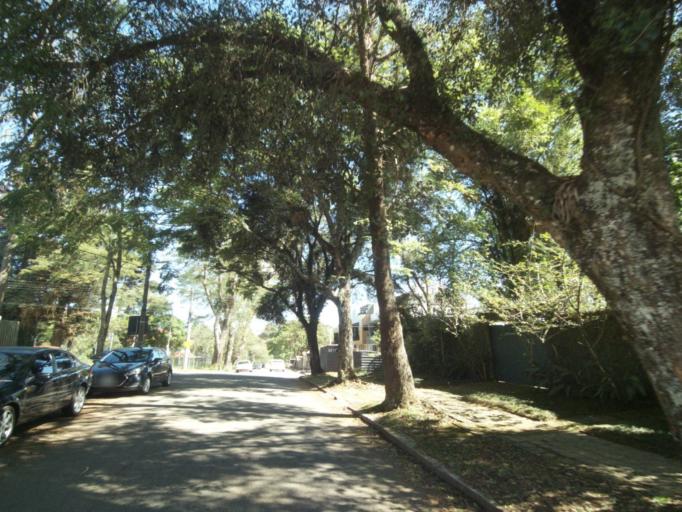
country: BR
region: Parana
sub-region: Curitiba
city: Curitiba
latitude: -25.3995
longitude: -49.2686
